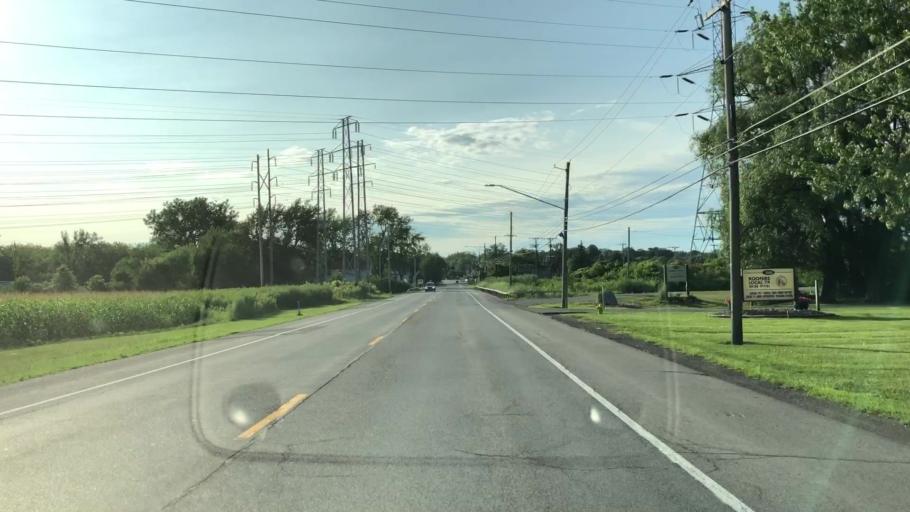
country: US
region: New York
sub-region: Erie County
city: West Seneca
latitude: 42.8642
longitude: -78.7705
